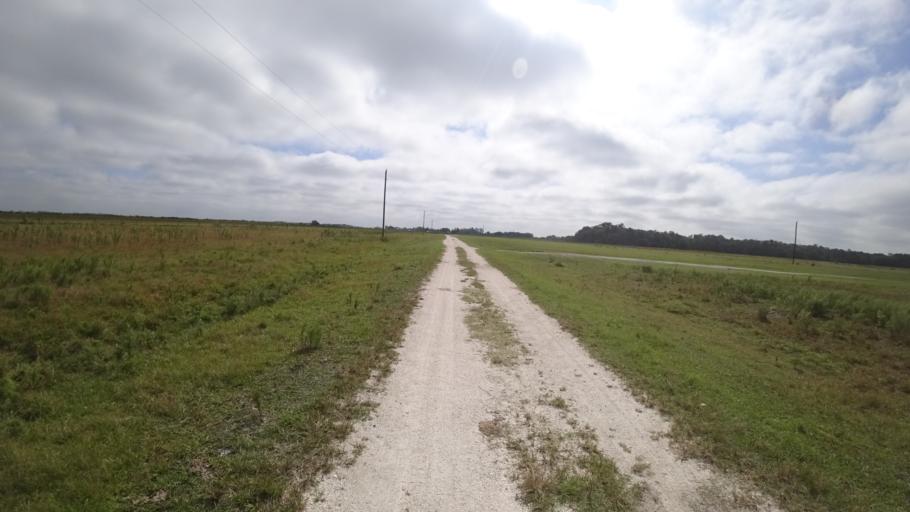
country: US
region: Florida
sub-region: DeSoto County
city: Arcadia
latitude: 27.3228
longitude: -82.1098
